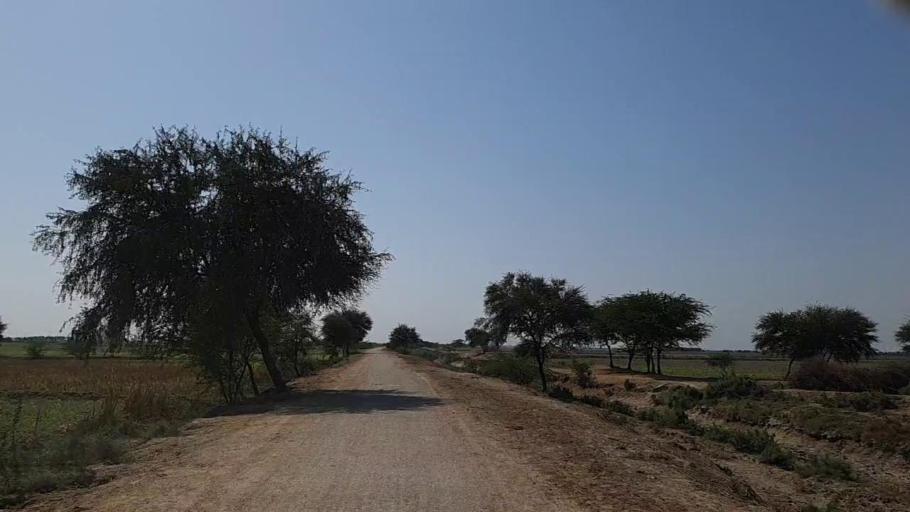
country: PK
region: Sindh
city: Mirpur Batoro
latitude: 24.6782
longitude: 68.3046
